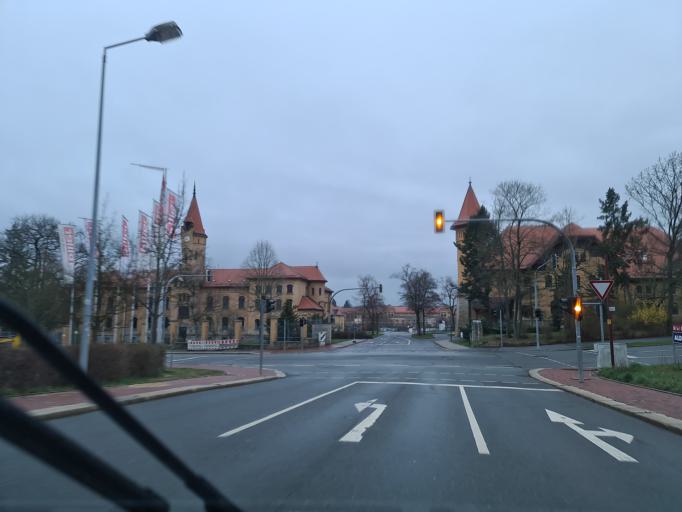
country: DE
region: Saxony
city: Plauen
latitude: 50.4945
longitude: 12.1014
